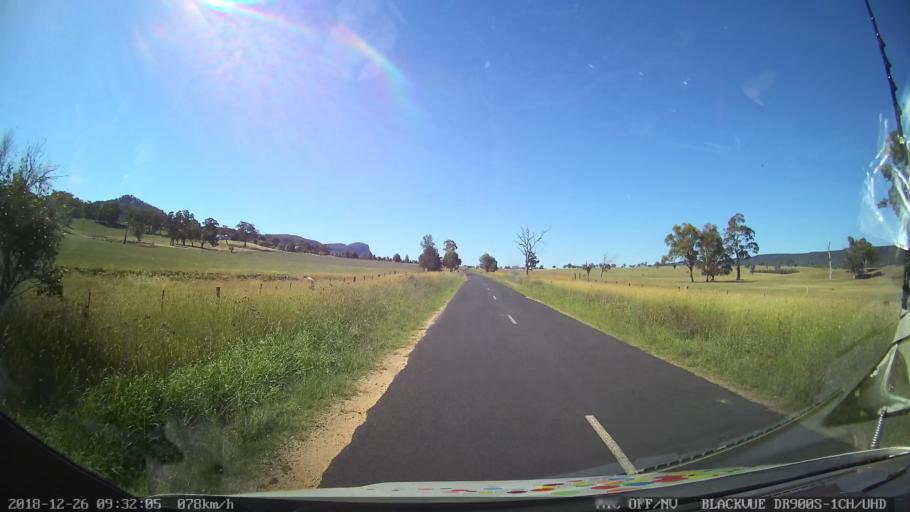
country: AU
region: New South Wales
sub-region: Mid-Western Regional
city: Kandos
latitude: -32.8802
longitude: 150.0321
